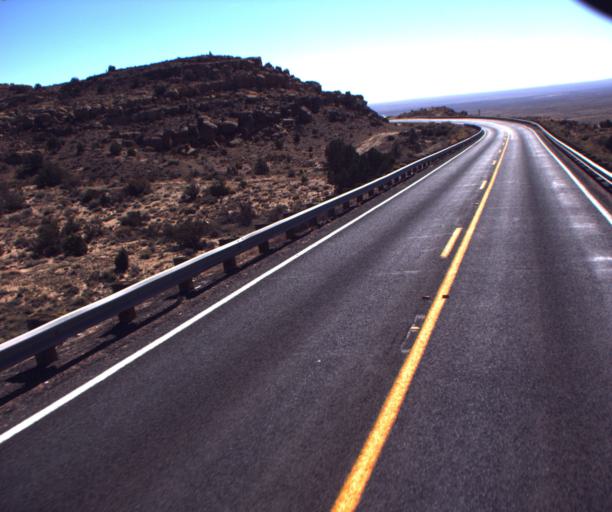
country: US
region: Arizona
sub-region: Navajo County
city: First Mesa
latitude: 35.8976
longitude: -110.6643
